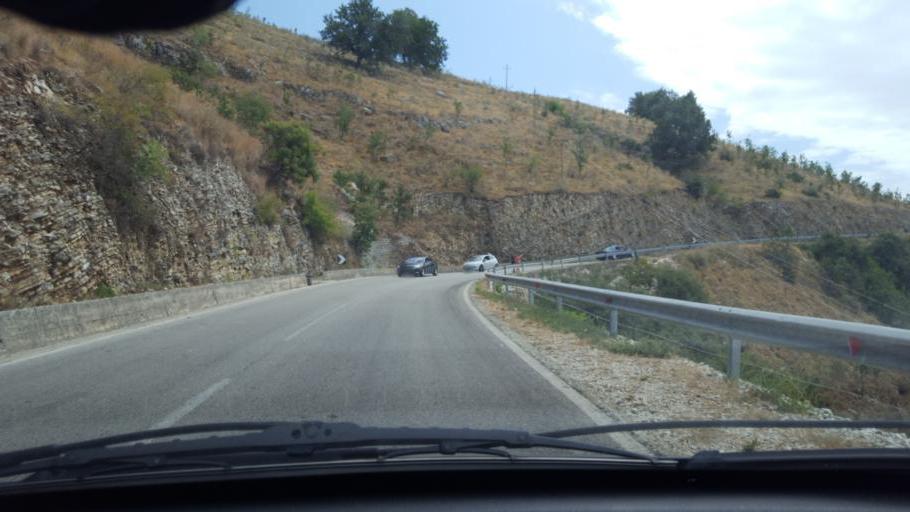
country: AL
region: Vlore
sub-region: Rrethi i Vlores
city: Himare
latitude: 40.0805
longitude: 19.7691
